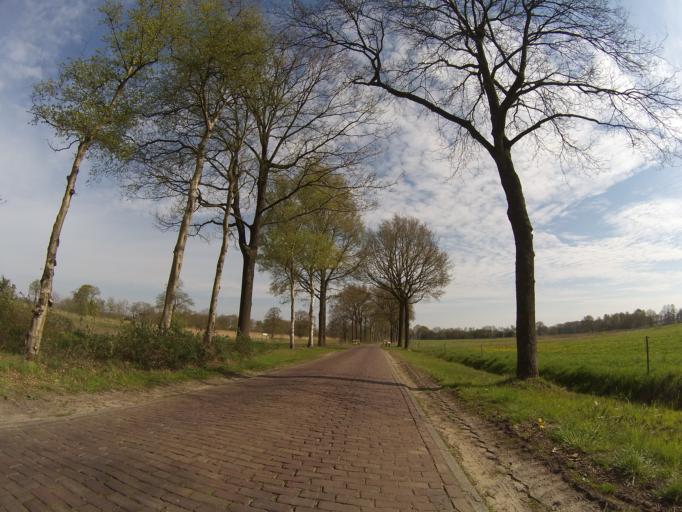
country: NL
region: Drenthe
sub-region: Gemeente Coevorden
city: Sleen
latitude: 52.8064
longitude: 6.7021
